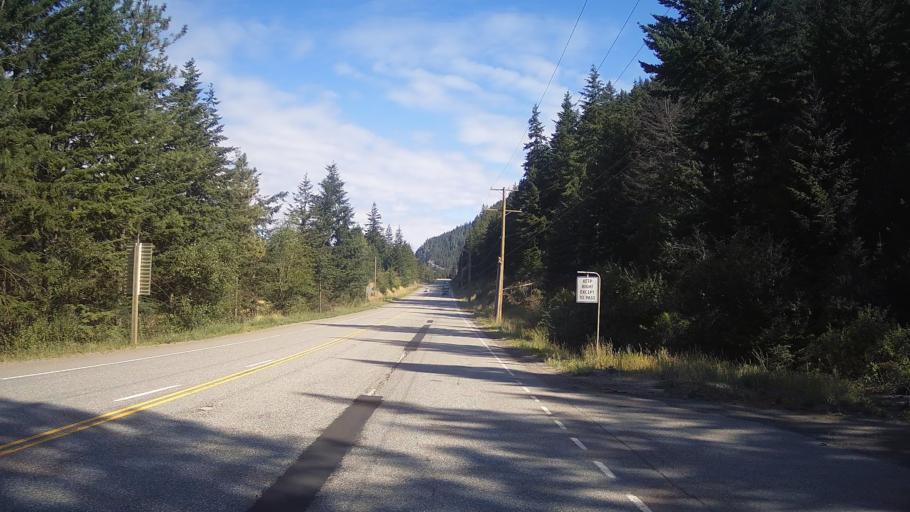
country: CA
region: British Columbia
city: Hope
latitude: 50.0544
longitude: -121.5422
